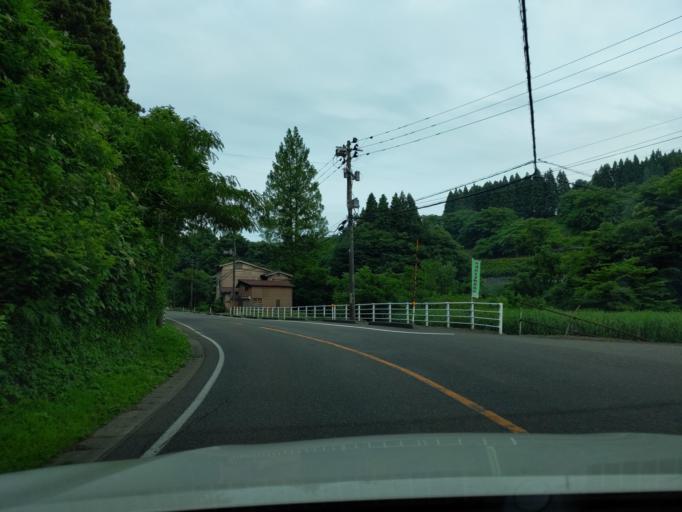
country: JP
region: Niigata
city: Nagaoka
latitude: 37.4375
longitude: 138.7138
